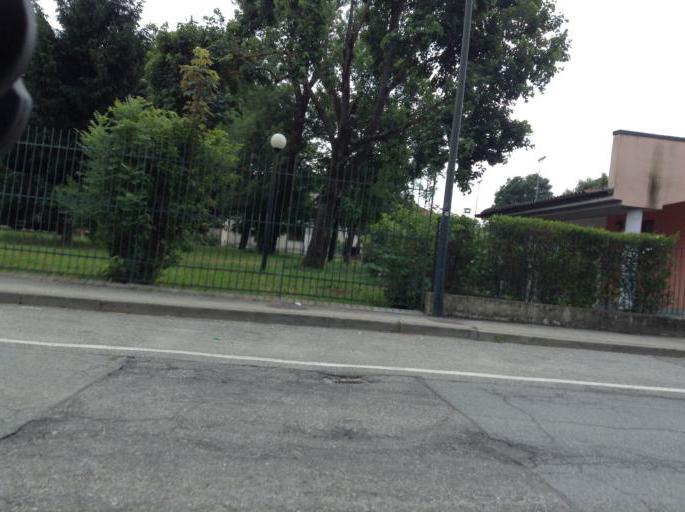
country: IT
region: Piedmont
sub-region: Provincia di Torino
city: Carignano
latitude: 44.9109
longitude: 7.6742
